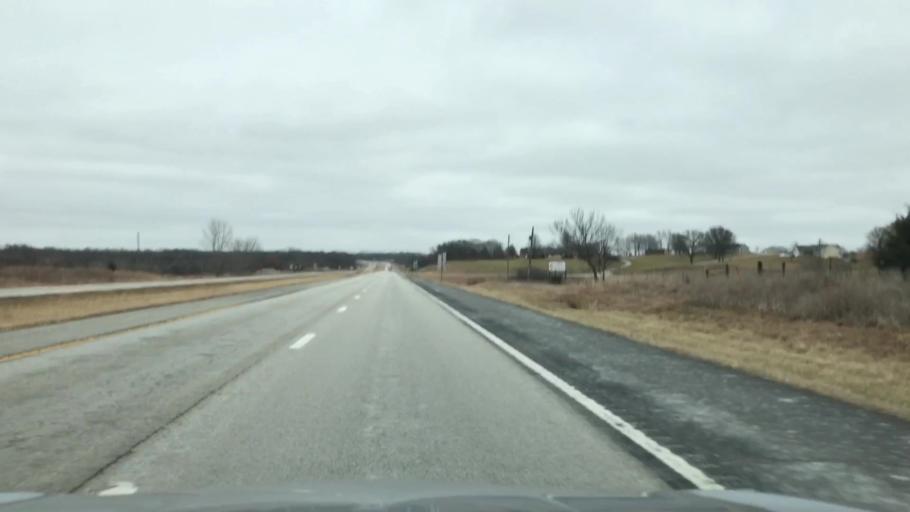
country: US
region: Missouri
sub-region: Caldwell County
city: Hamilton
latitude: 39.7435
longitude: -94.0416
